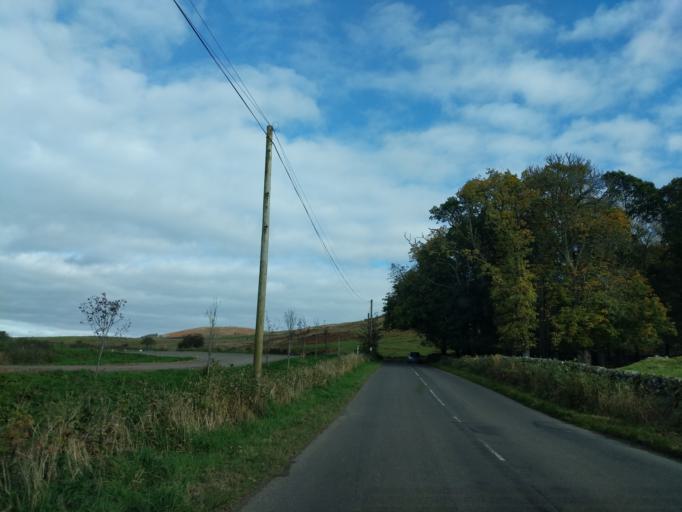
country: GB
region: Scotland
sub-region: Dumfries and Galloway
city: Thornhill
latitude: 55.1932
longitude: -3.8527
